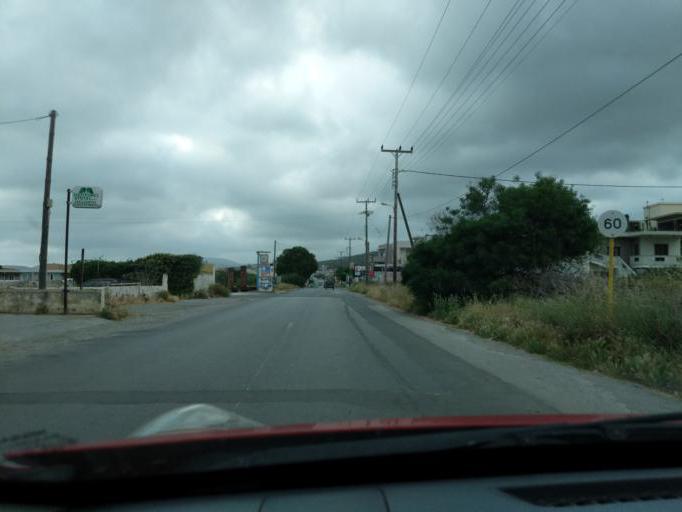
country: GR
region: Crete
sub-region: Nomos Chanias
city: Kissamos
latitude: 35.4992
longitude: 23.6452
